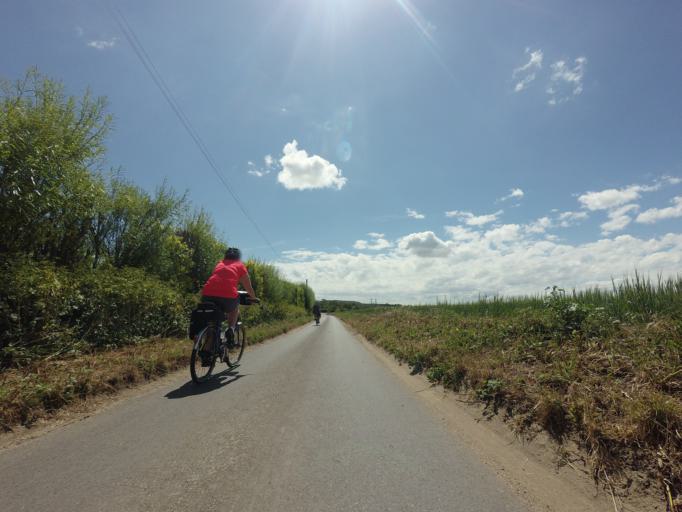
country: GB
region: England
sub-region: Medway
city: Cooling
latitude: 51.4548
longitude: 0.5111
